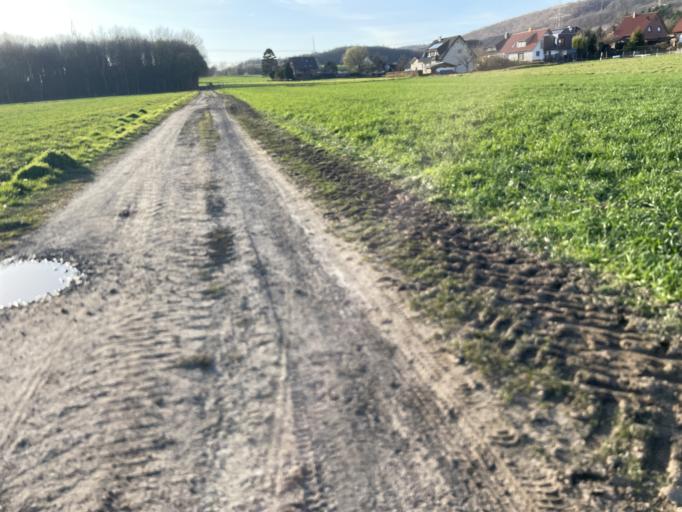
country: DE
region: North Rhine-Westphalia
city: Porta Westfalica
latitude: 52.2283
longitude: 8.9736
